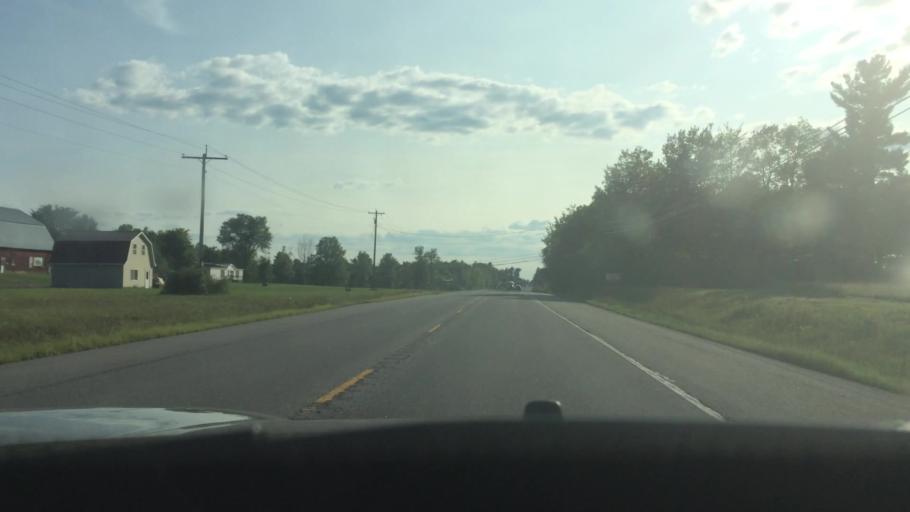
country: US
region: New York
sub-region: St. Lawrence County
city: Potsdam
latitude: 44.6427
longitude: -75.0622
